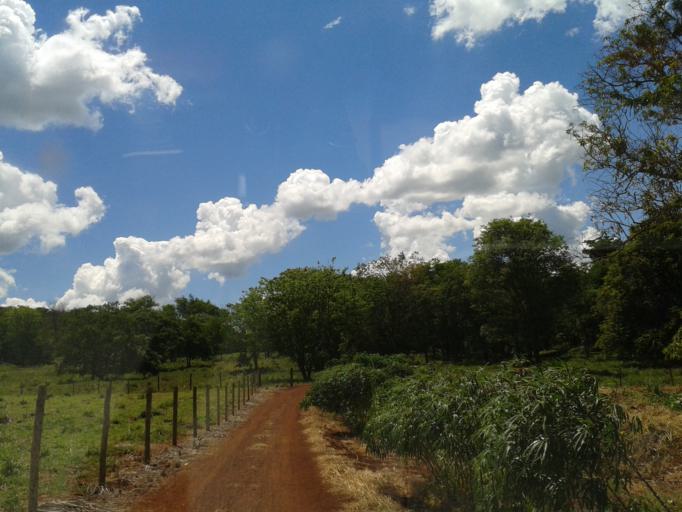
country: BR
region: Minas Gerais
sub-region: Centralina
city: Centralina
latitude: -18.6906
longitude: -49.1780
